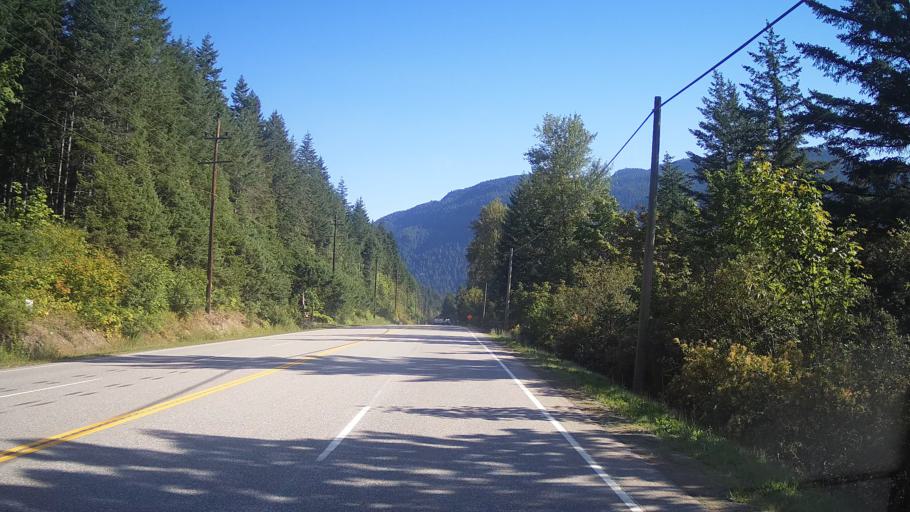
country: CA
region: British Columbia
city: Hope
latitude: 49.6799
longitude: -121.4175
